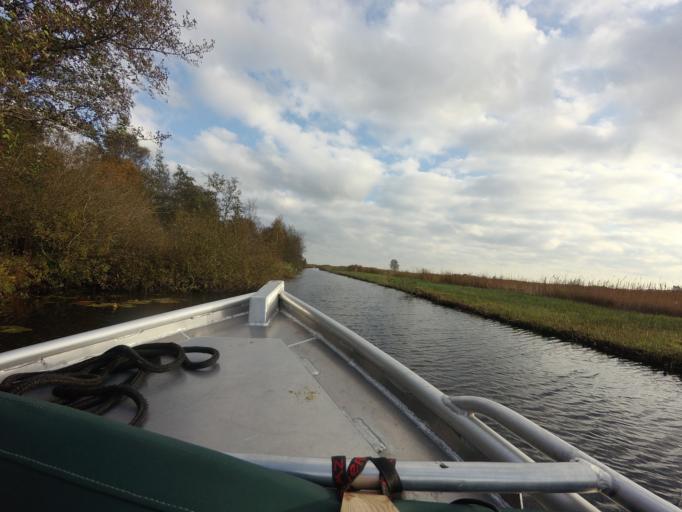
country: NL
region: Overijssel
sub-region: Gemeente Steenwijkerland
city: Blokzijl
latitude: 52.7592
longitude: 5.9488
